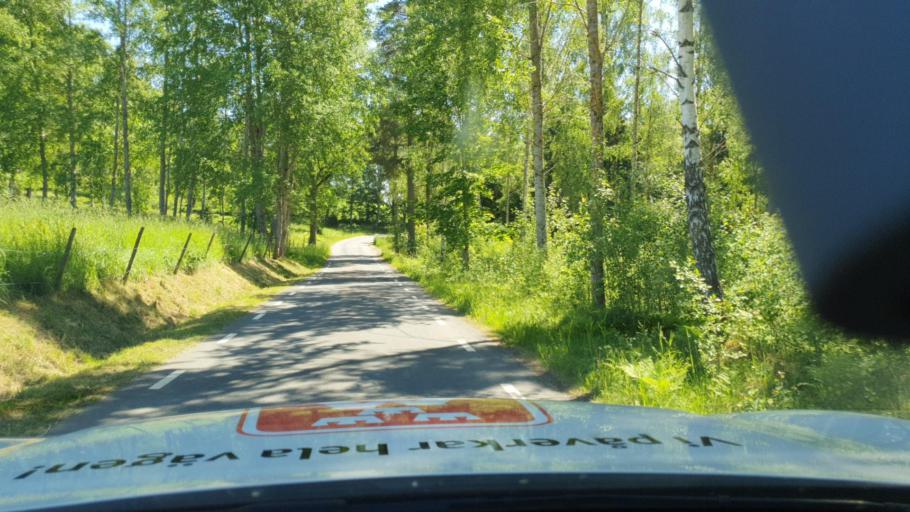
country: SE
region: Joenkoeping
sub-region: Habo Kommun
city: Habo
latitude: 57.9054
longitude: 14.0487
